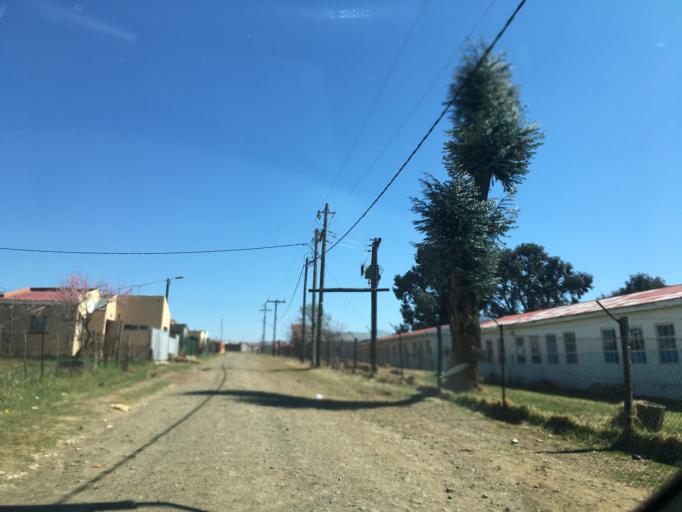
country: ZA
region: Eastern Cape
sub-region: Chris Hani District Municipality
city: Elliot
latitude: -31.3293
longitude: 27.8267
